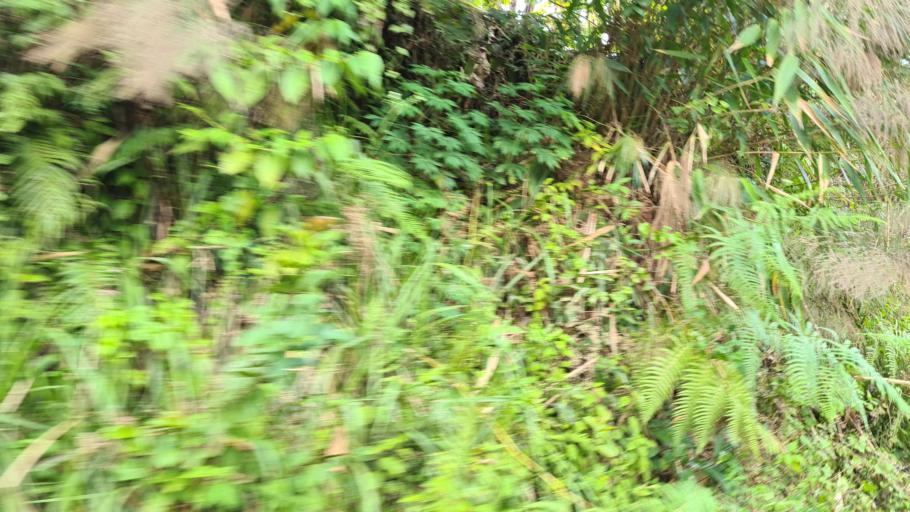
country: ID
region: Lampung
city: Kenali
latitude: -5.0596
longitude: 104.4106
